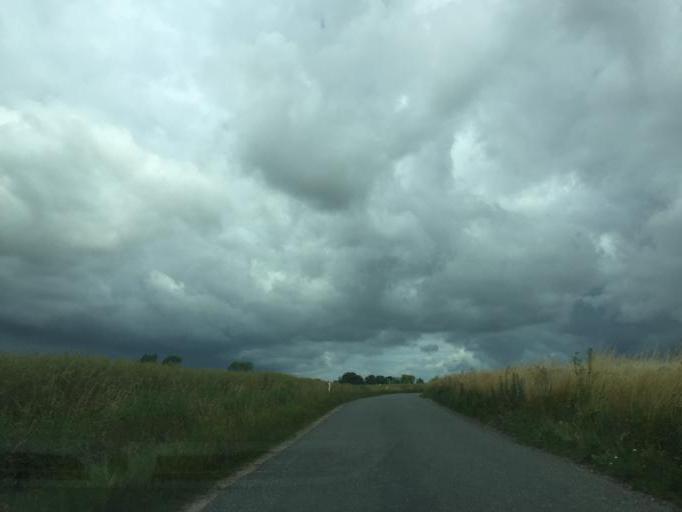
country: DK
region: South Denmark
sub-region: Faaborg-Midtfyn Kommune
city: Arslev
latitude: 55.2933
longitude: 10.4727
